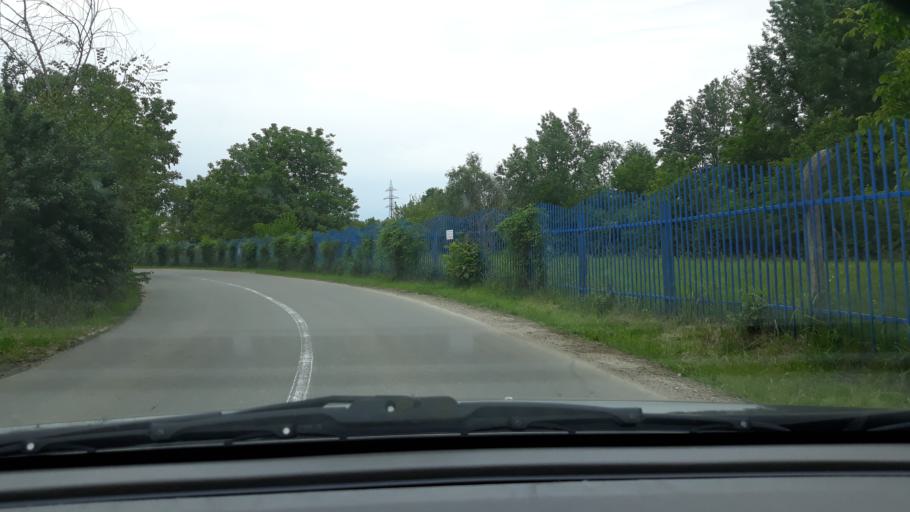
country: RO
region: Bihor
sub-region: Comuna Sanmartin
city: Sanmartin
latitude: 47.0504
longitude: 21.9821
